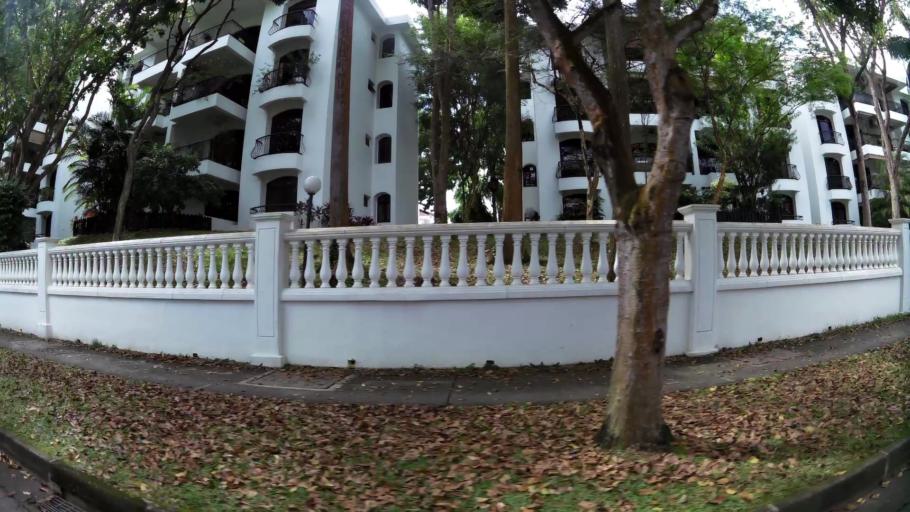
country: SG
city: Singapore
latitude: 1.3005
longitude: 103.8168
